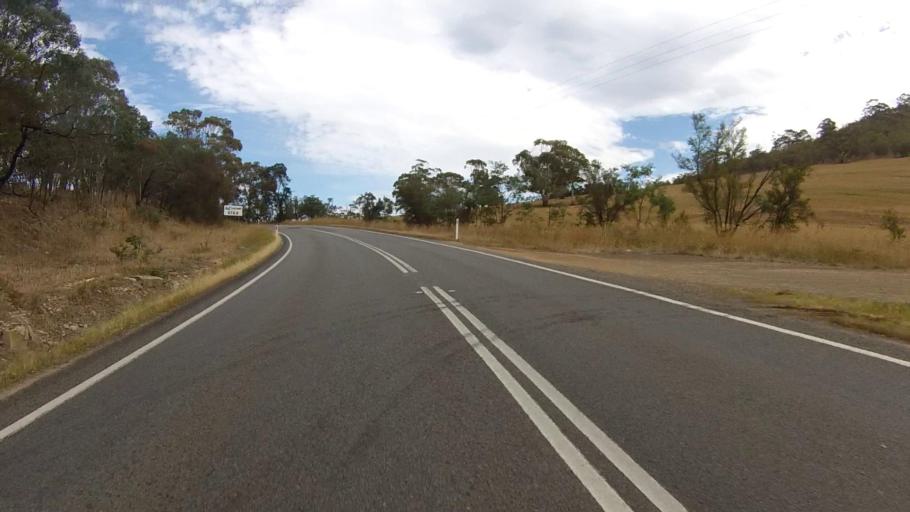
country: AU
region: Tasmania
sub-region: Sorell
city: Sorell
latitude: -42.7061
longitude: 147.5005
